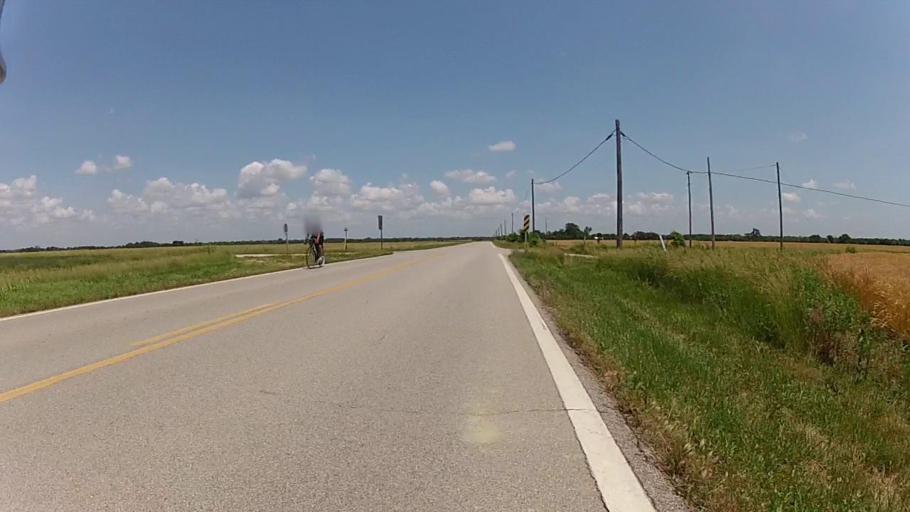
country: US
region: Kansas
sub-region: Labette County
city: Altamont
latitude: 37.1926
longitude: -95.4324
